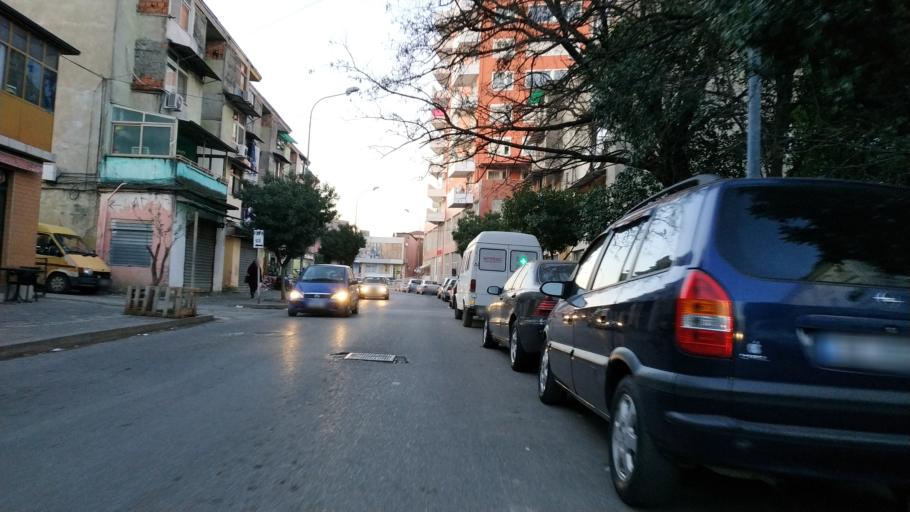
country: AL
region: Shkoder
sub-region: Rrethi i Shkodres
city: Shkoder
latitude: 42.0751
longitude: 19.5183
